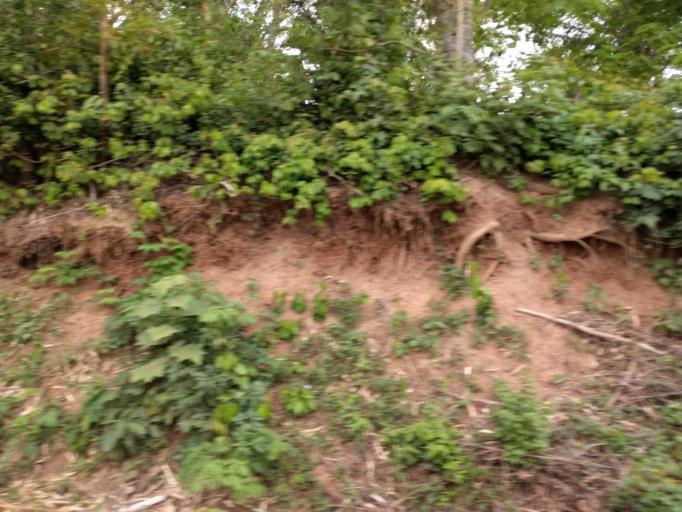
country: BO
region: Santa Cruz
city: Santiago del Torno
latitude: -17.9299
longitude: -63.4221
